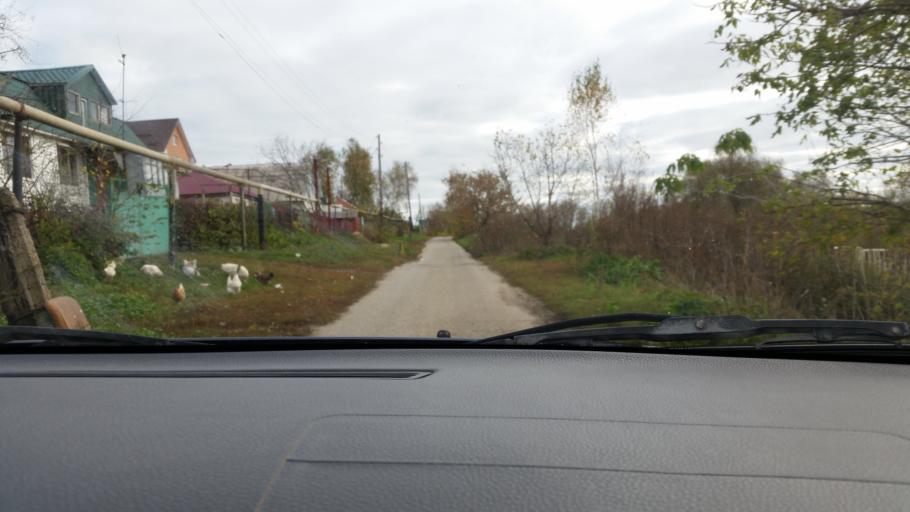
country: RU
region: Lipetsk
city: Gryazi
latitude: 52.4519
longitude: 39.9835
